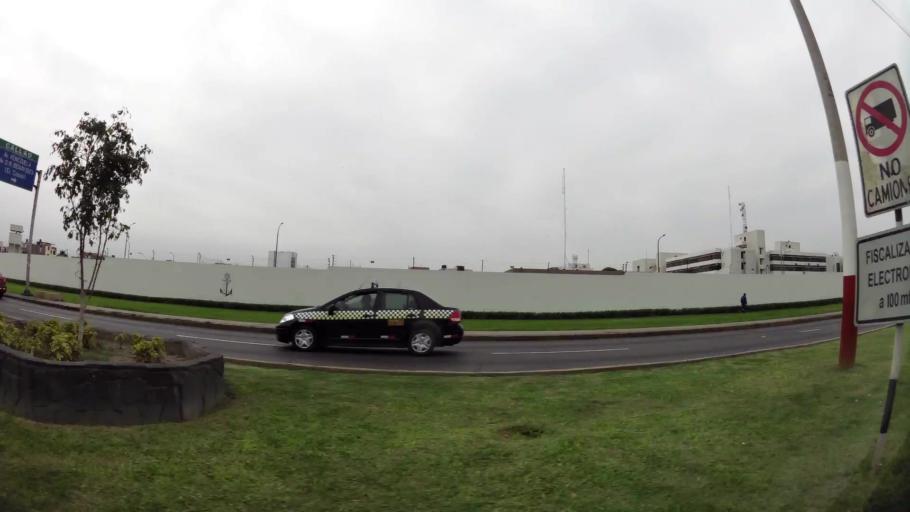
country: PE
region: Callao
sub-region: Callao
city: Callao
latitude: -12.0706
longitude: -77.1086
